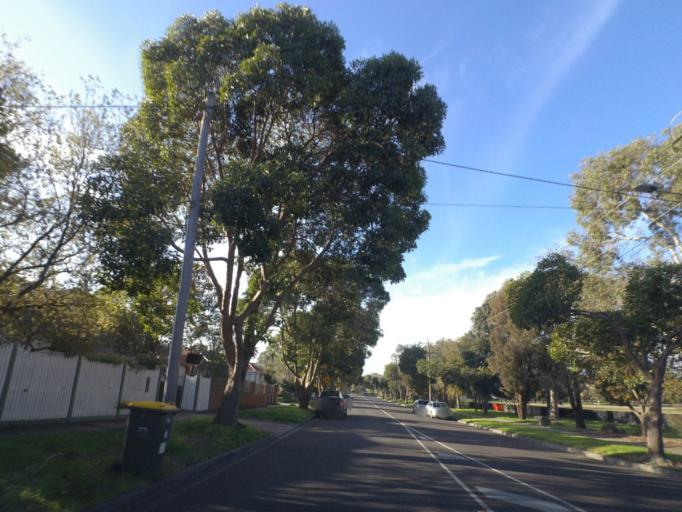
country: AU
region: Victoria
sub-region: Whitehorse
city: Box Hill North
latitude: -37.8098
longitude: 145.1323
